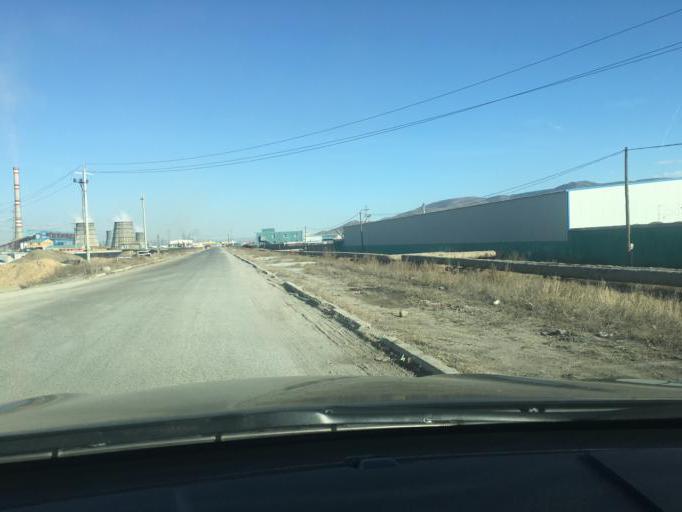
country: MN
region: Ulaanbaatar
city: Ulaanbaatar
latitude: 47.8879
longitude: 106.7800
